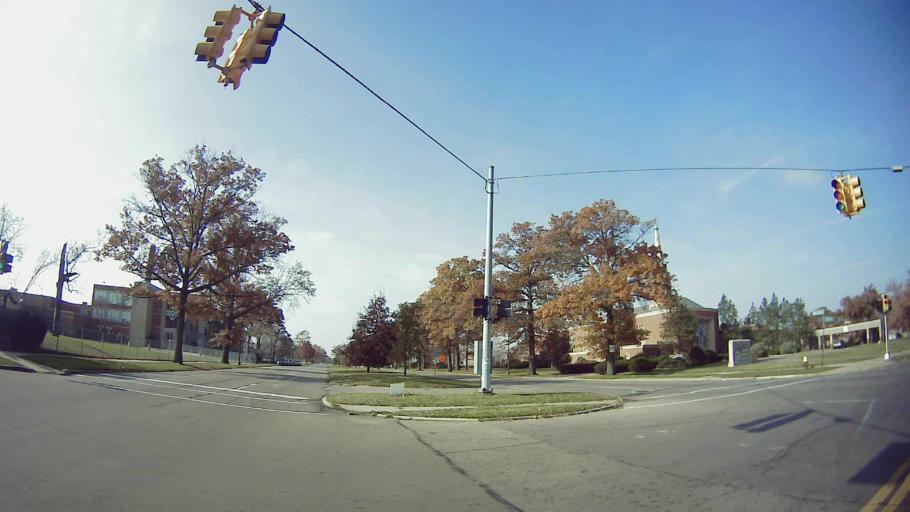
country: US
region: Michigan
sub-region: Oakland County
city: Oak Park
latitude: 42.4200
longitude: -83.1896
